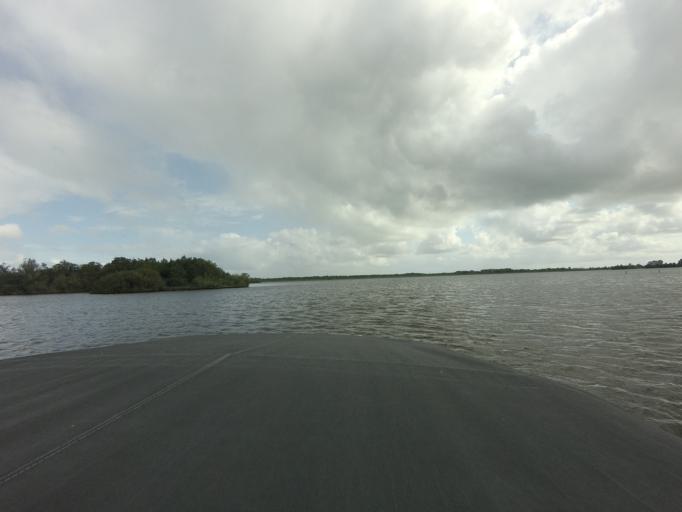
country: NL
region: Friesland
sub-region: Gemeente Boarnsterhim
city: Warten
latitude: 53.1159
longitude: 5.9287
